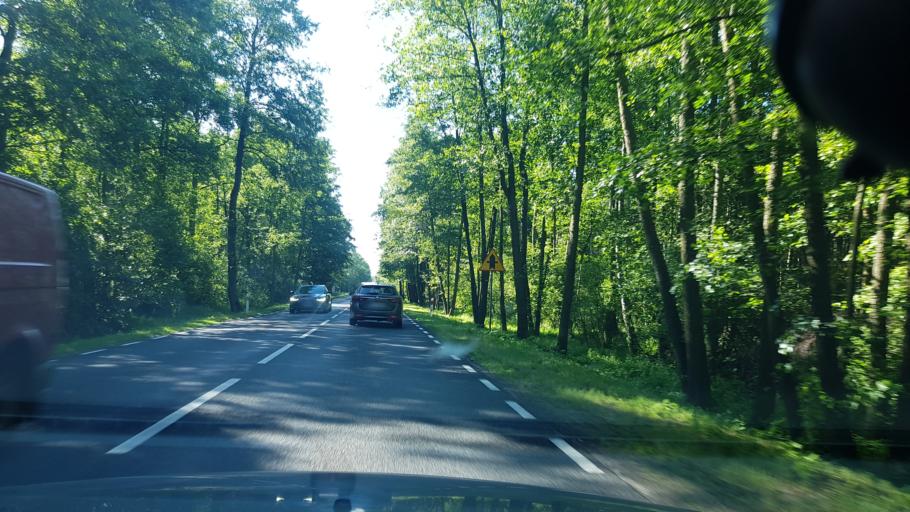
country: PL
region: Masovian Voivodeship
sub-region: Powiat wyszkowski
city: Branszczyk
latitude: 52.5783
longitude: 21.5354
